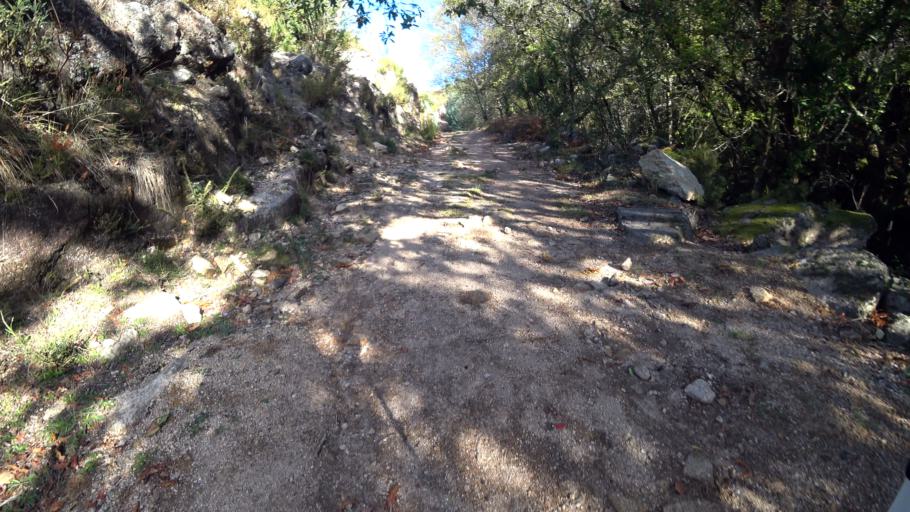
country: PT
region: Braga
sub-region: Vieira do Minho
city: Real
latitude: 41.7677
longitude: -8.1819
